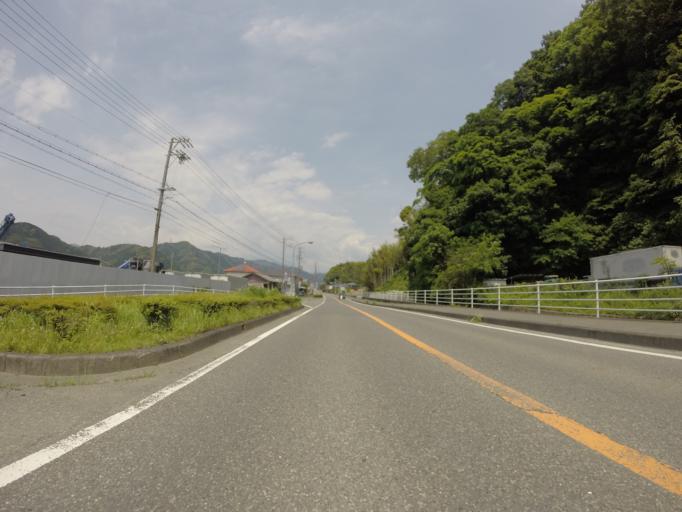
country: JP
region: Shizuoka
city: Shizuoka-shi
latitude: 35.0468
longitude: 138.3756
